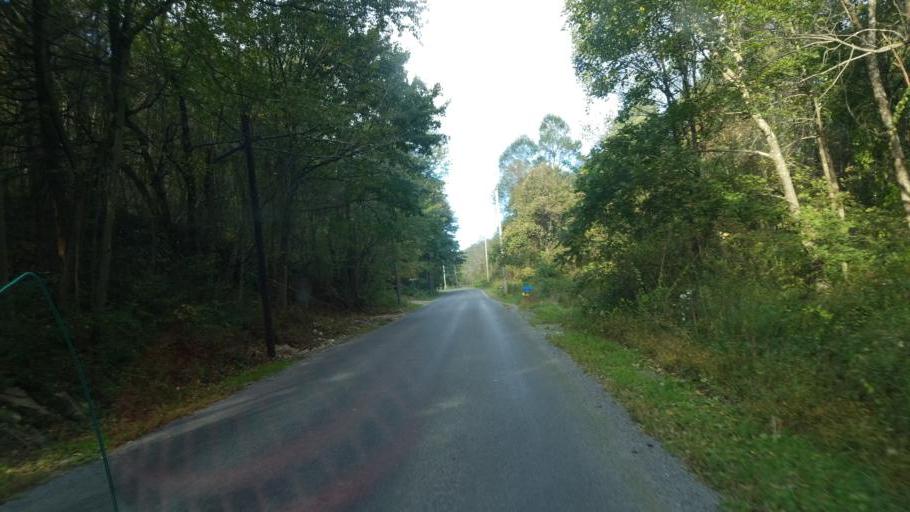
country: US
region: Pennsylvania
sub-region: Franklin County
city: Fayetteville
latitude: 39.8967
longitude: -77.4118
